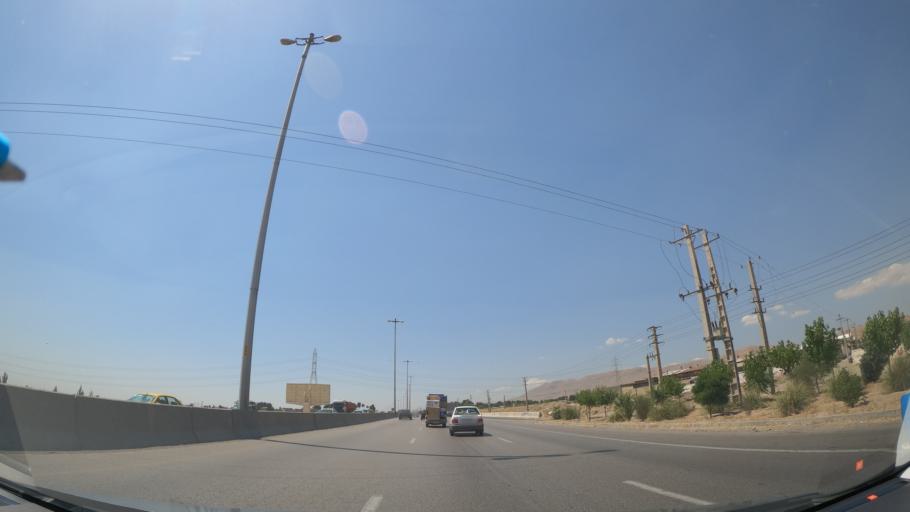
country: IR
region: Alborz
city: Karaj
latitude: 35.8693
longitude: 50.8991
